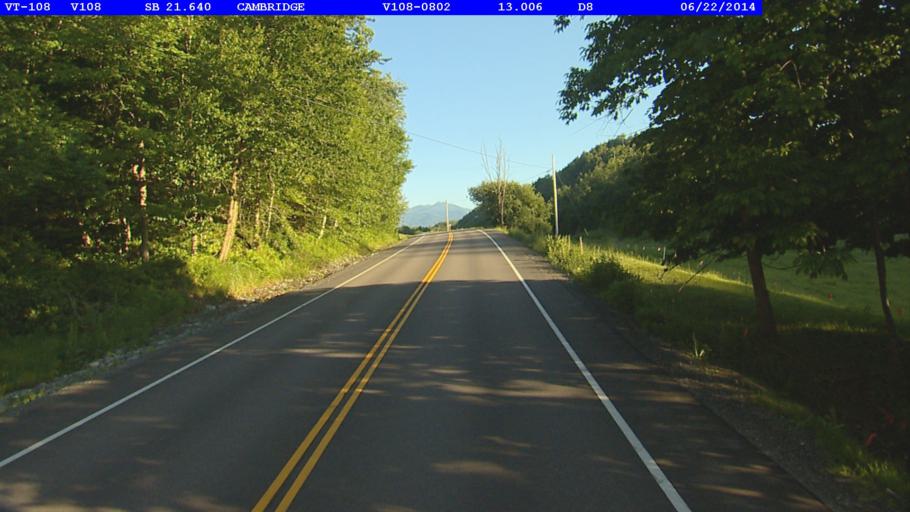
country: US
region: Vermont
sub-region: Lamoille County
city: Johnson
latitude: 44.7022
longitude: -72.8303
